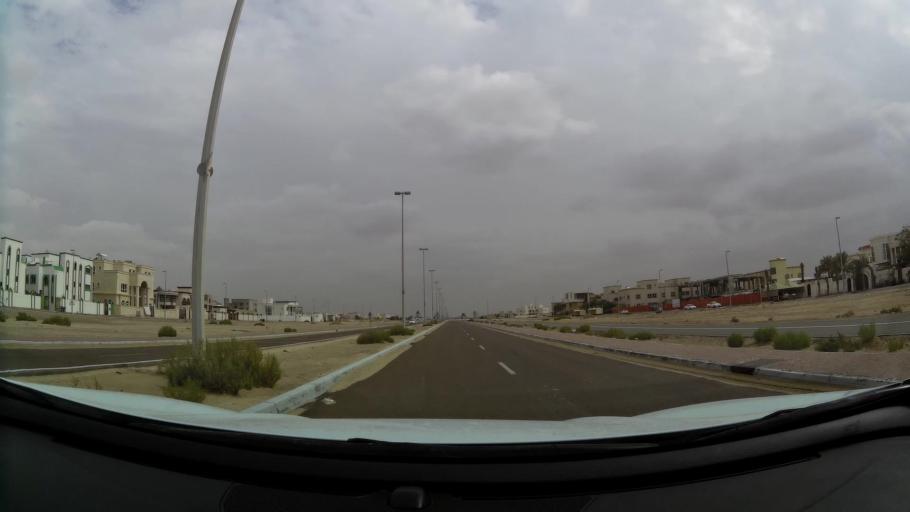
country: AE
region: Abu Dhabi
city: Abu Dhabi
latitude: 24.3880
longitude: 54.6422
